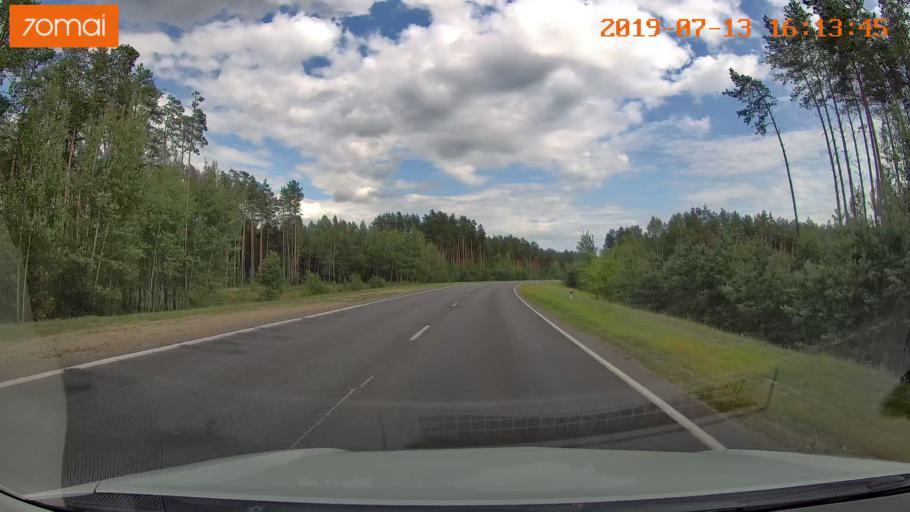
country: BY
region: Mogilev
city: Babruysk
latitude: 53.1611
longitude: 29.3103
